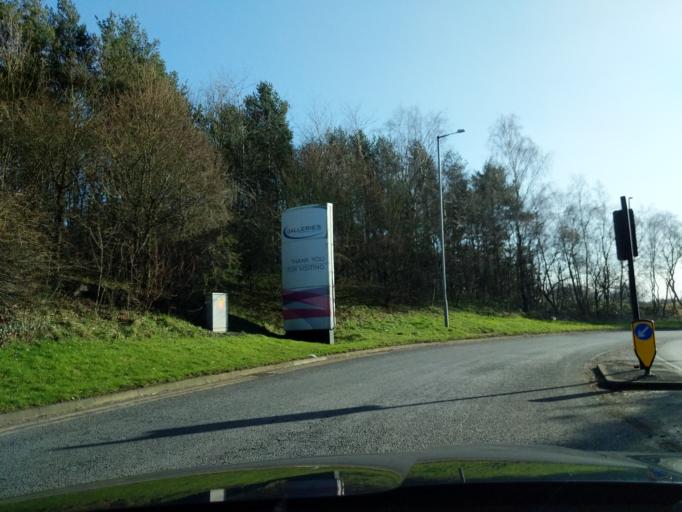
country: GB
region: England
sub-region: Sunderland
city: Washington
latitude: 54.8968
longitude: -1.5333
